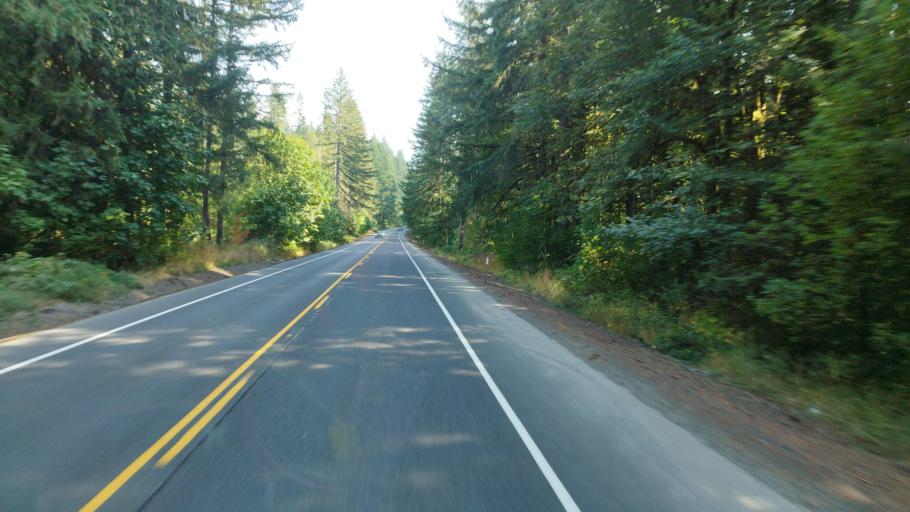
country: US
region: Oregon
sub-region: Columbia County
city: Vernonia
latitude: 45.7765
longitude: -123.3314
